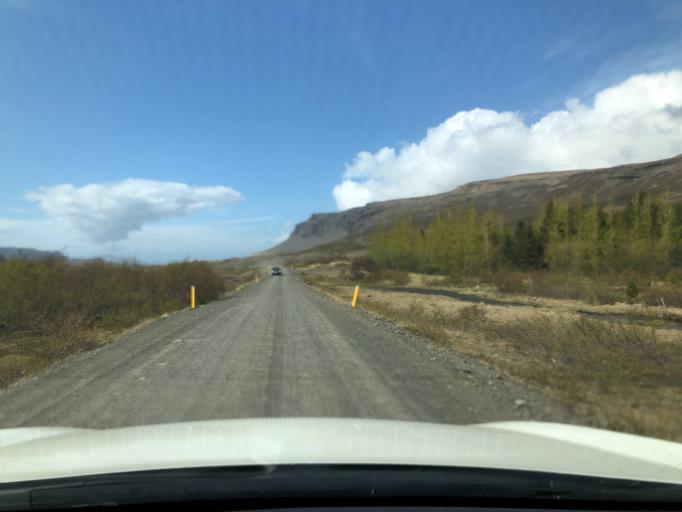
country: IS
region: South
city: Hveragerdi
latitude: 64.3855
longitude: -21.3263
